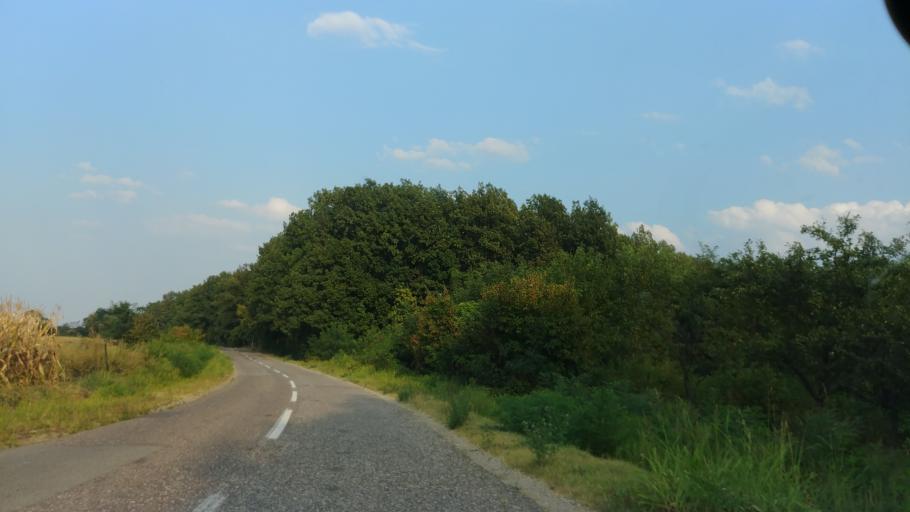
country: BA
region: Republika Srpska
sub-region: Opstina Ugljevik
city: Ugljevik
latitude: 44.7064
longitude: 18.9720
